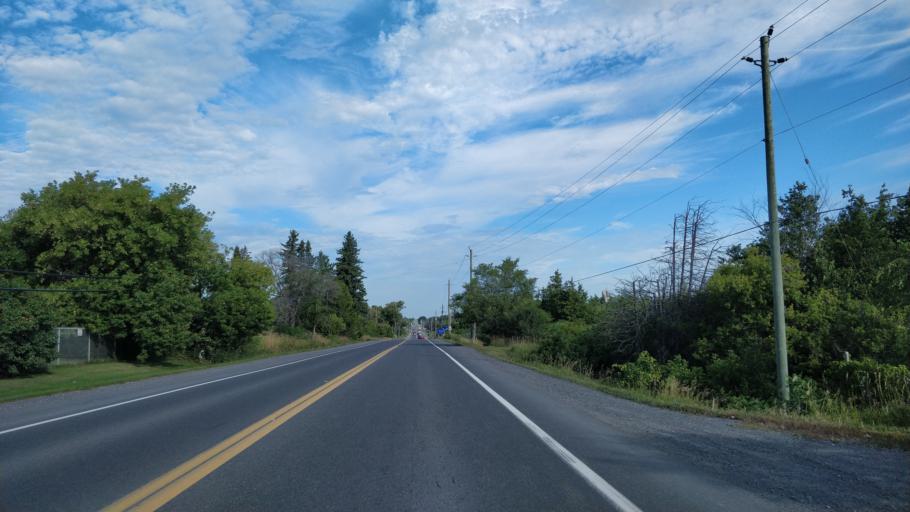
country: CA
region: Ontario
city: Bells Corners
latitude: 45.2865
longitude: -75.9639
